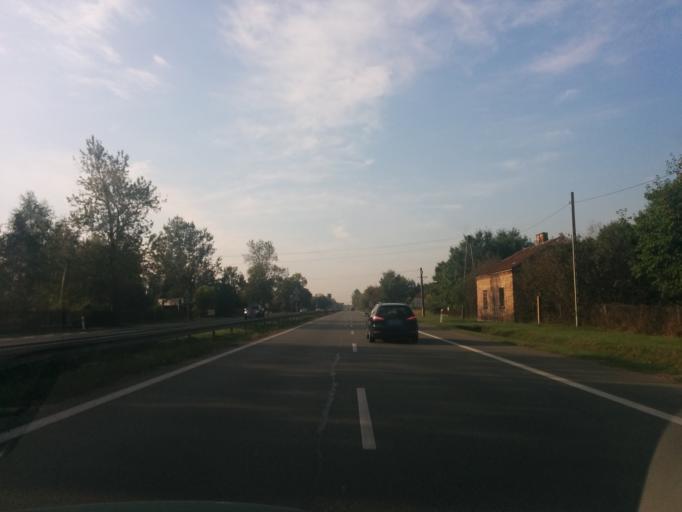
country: PL
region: Masovian Voivodeship
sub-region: Powiat piaseczynski
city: Tarczyn
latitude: 52.0459
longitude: 20.8639
